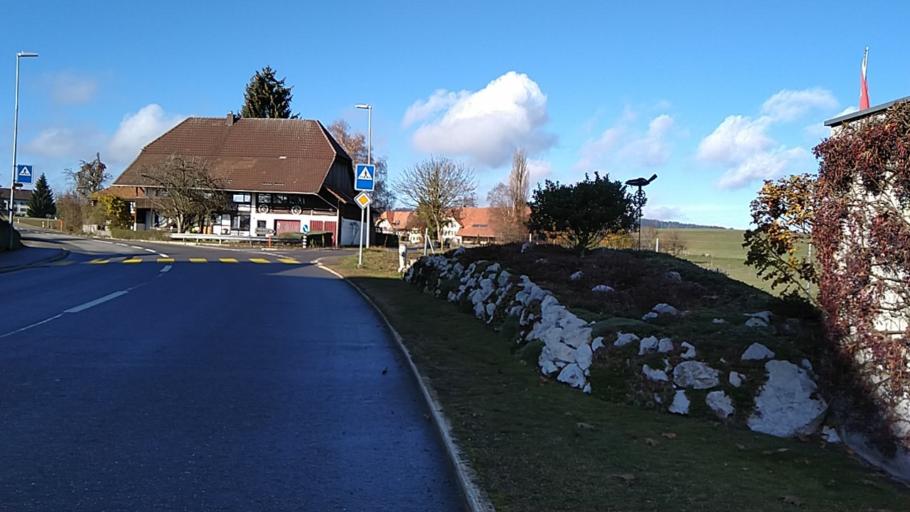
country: CH
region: Bern
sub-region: Bern-Mittelland District
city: Wohlen
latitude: 46.9882
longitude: 7.3824
